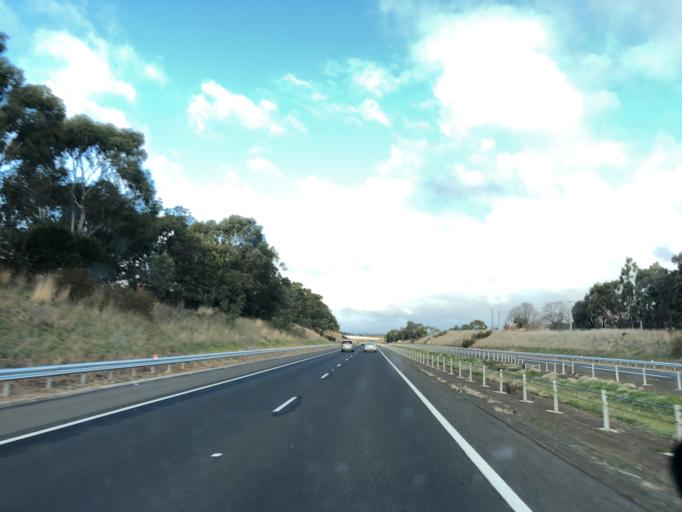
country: AU
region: Victoria
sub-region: Mount Alexander
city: Castlemaine
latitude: -37.2349
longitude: 144.4512
